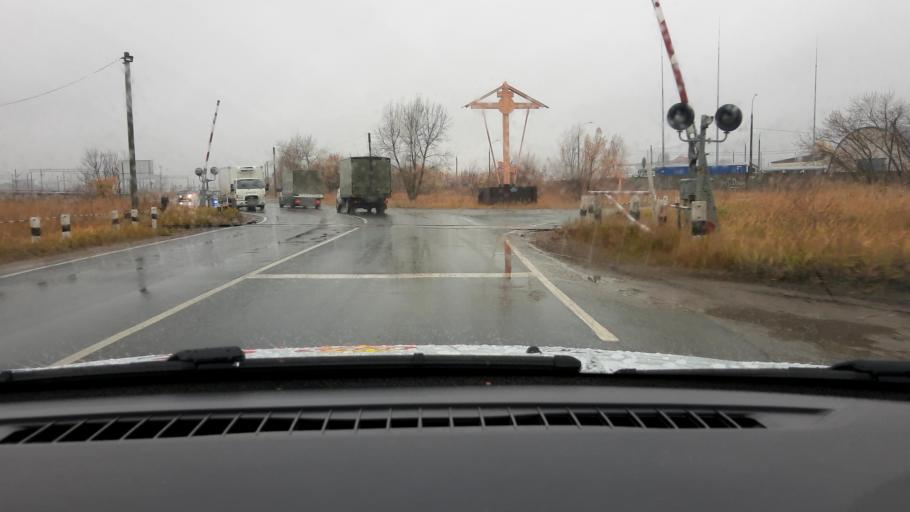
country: RU
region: Nizjnij Novgorod
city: Babino
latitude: 56.2555
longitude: 43.5954
